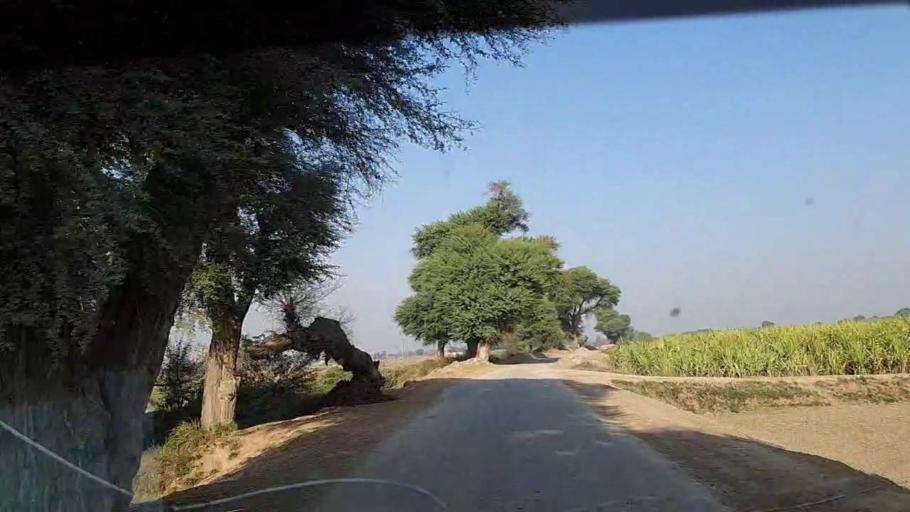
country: PK
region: Sindh
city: Sobhadero
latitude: 27.2428
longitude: 68.3224
